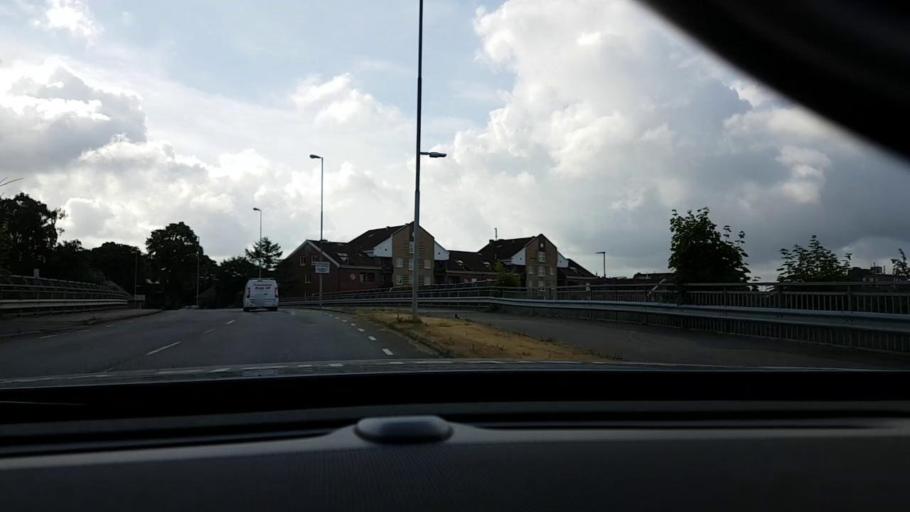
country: SE
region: Skane
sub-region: Hassleholms Kommun
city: Hassleholm
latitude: 56.1609
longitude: 13.7642
